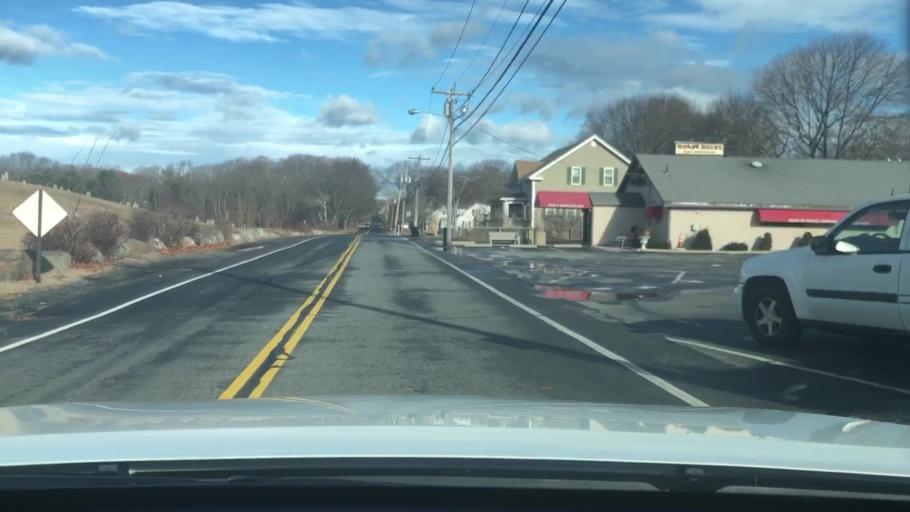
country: US
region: Rhode Island
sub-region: Providence County
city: Woonsocket
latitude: 42.0169
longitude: -71.5136
